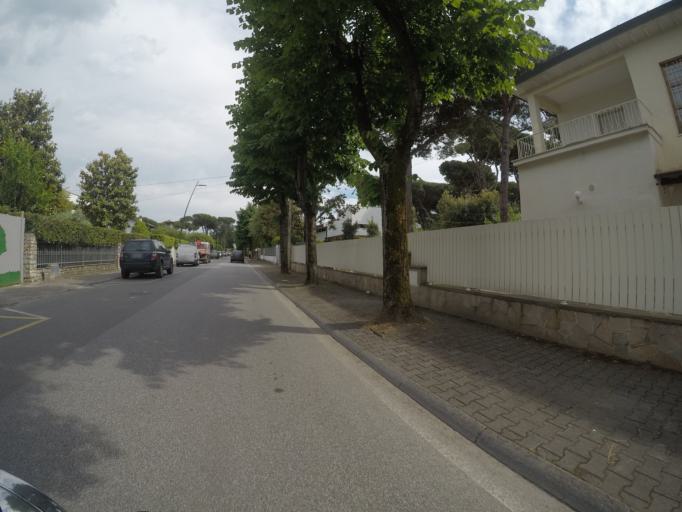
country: IT
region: Tuscany
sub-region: Provincia di Lucca
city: Forte dei Marmi
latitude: 43.9718
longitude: 10.1541
